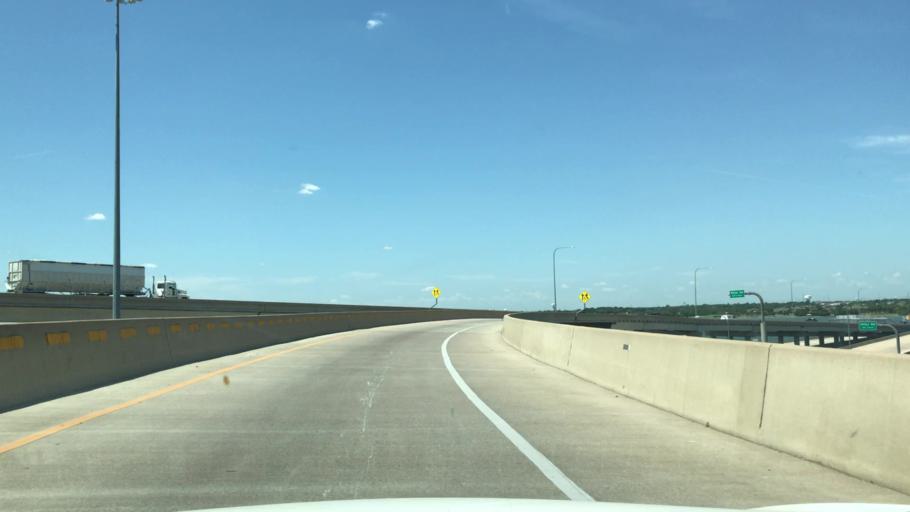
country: US
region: Texas
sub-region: Dallas County
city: Rowlett
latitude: 32.8608
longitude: -96.5544
